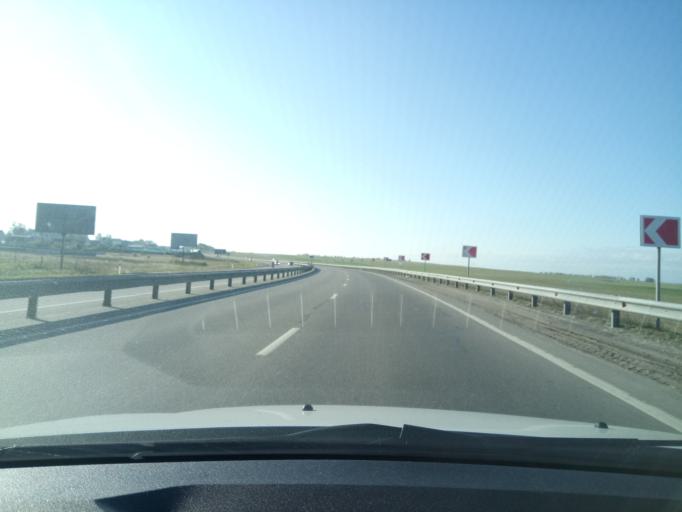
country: RU
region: Nizjnij Novgorod
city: Burevestnik
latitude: 56.1524
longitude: 43.9086
